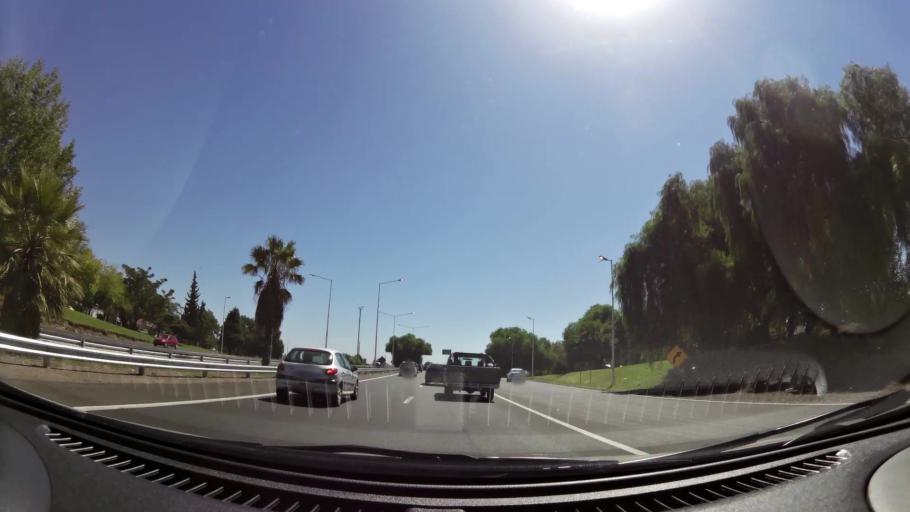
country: AR
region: Mendoza
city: Mendoza
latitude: -32.8992
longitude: -68.8193
